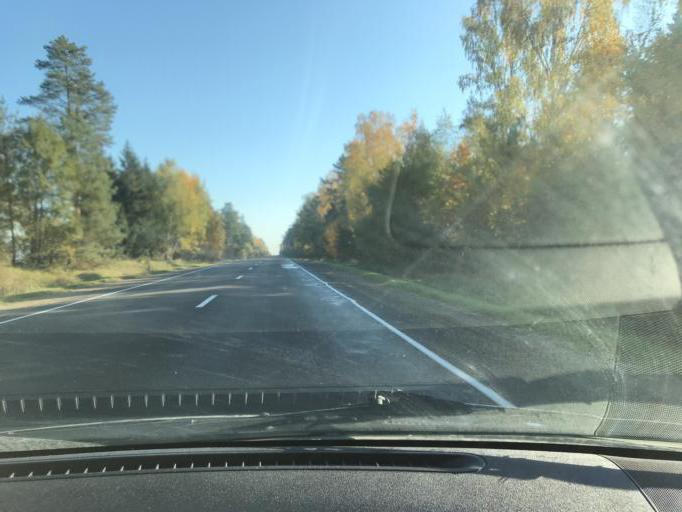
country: BY
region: Brest
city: Lyakhavichy
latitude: 52.9594
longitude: 26.3785
